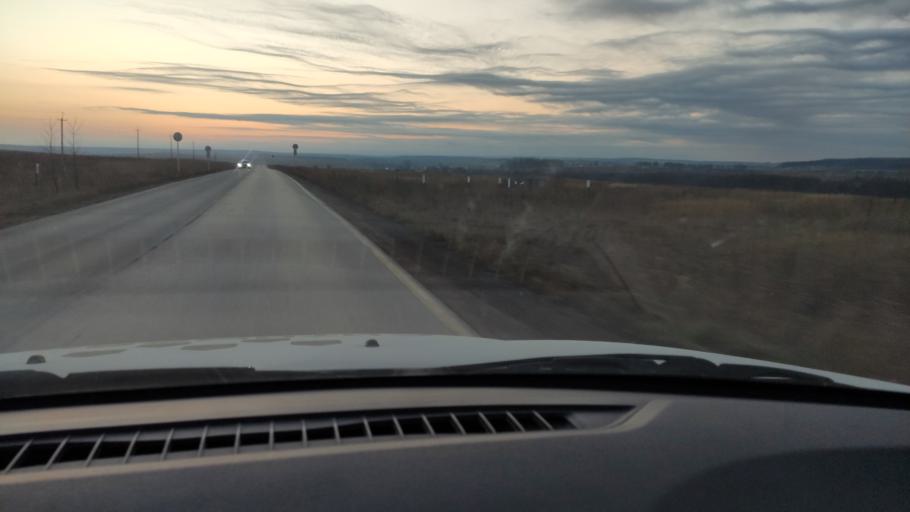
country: RU
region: Perm
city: Lobanovo
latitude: 57.8060
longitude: 56.3398
